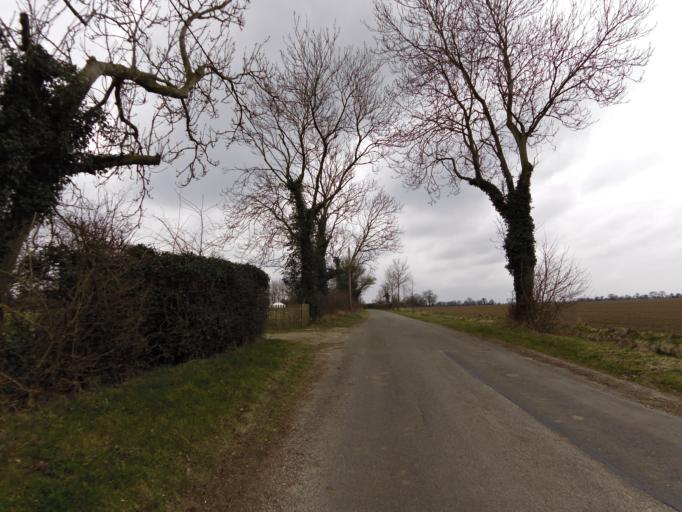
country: GB
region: England
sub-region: Suffolk
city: Halesworth
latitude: 52.3910
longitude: 1.5188
